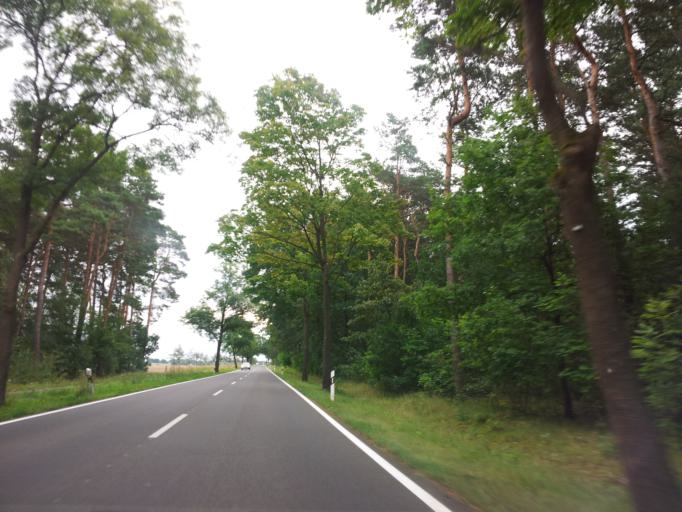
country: DE
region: Brandenburg
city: Treuenbrietzen
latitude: 52.0948
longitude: 12.8185
